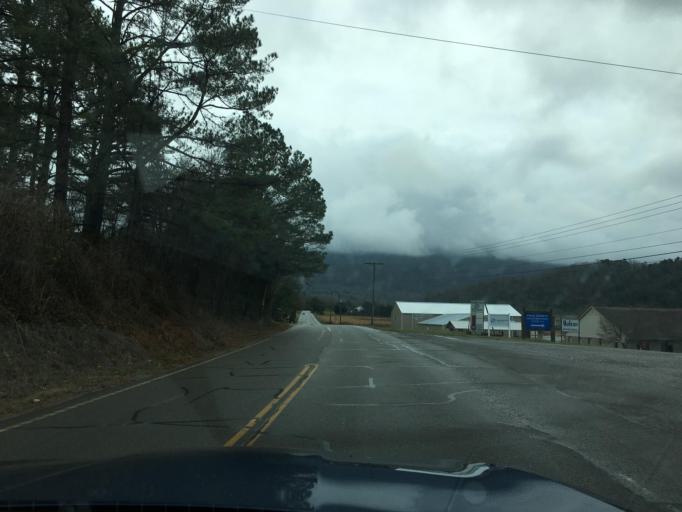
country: US
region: Tennessee
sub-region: Polk County
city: Benton
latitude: 35.1696
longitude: -84.6425
